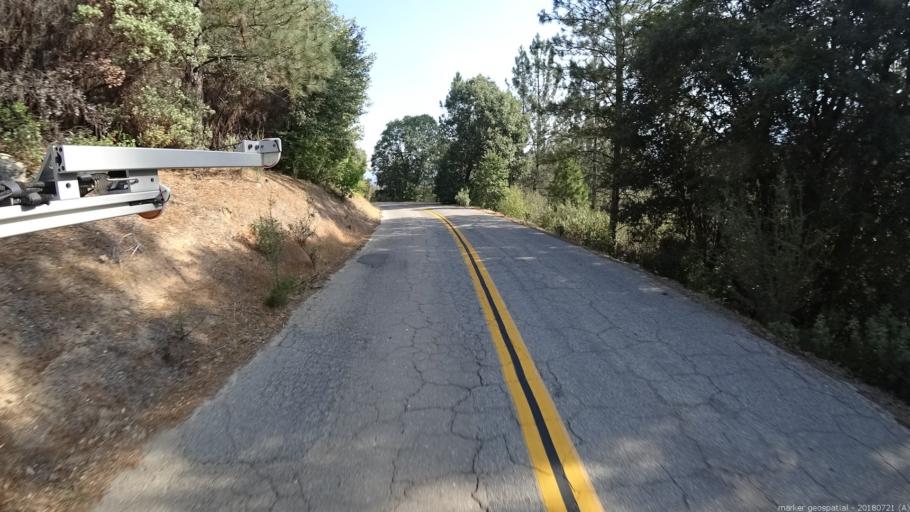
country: US
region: California
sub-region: Madera County
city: Oakhurst
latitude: 37.2573
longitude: -119.5261
